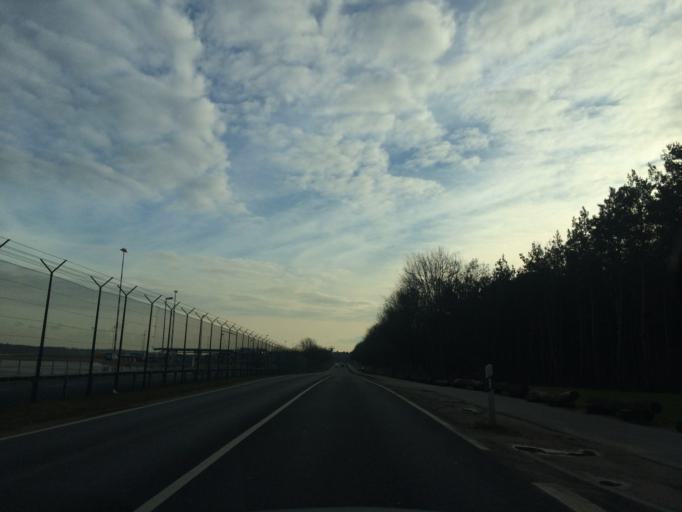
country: DE
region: Hesse
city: Kelsterbach
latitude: 50.0335
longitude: 8.5202
